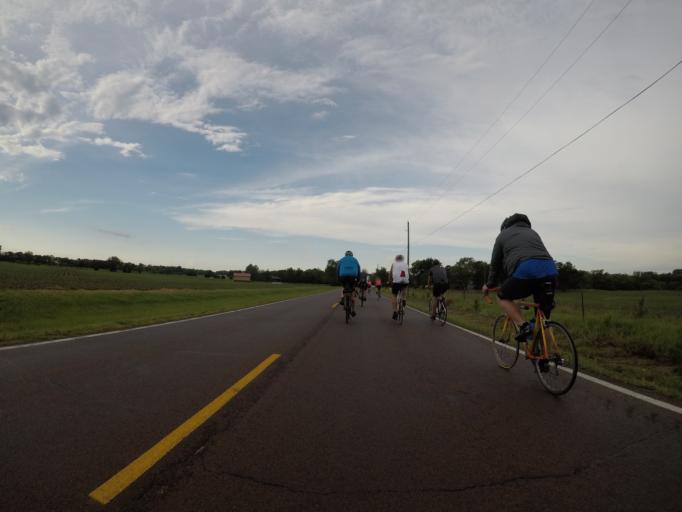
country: US
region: Kansas
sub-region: Shawnee County
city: Topeka
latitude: 38.9760
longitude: -95.7133
